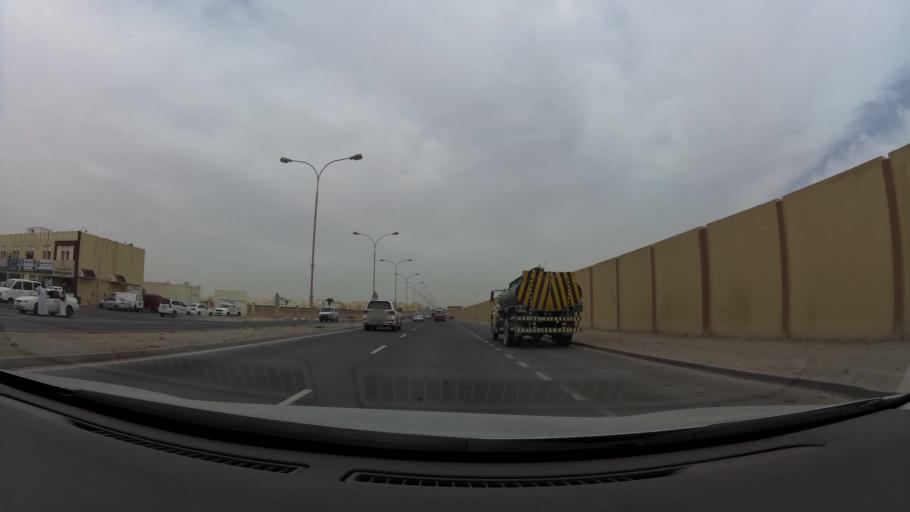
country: QA
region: Baladiyat ar Rayyan
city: Ar Rayyan
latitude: 25.2250
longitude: 51.4503
